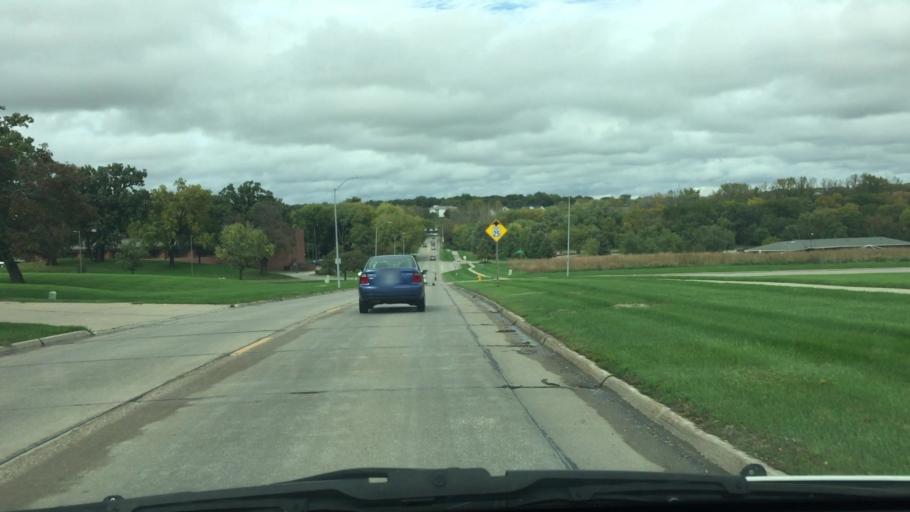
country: US
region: Iowa
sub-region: Polk County
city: Clive
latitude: 41.6062
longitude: -93.7749
